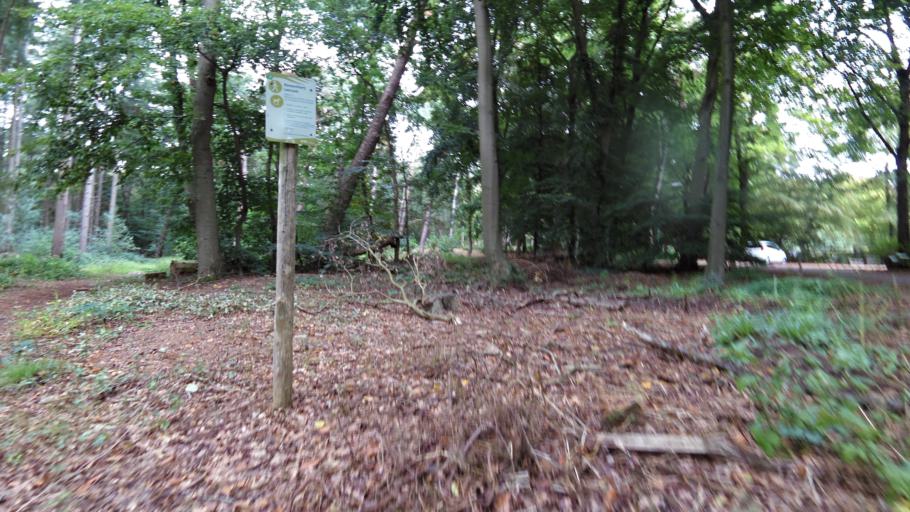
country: NL
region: Utrecht
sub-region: Gemeente Utrechtse Heuvelrug
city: Leersum
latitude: 52.0165
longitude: 5.4181
